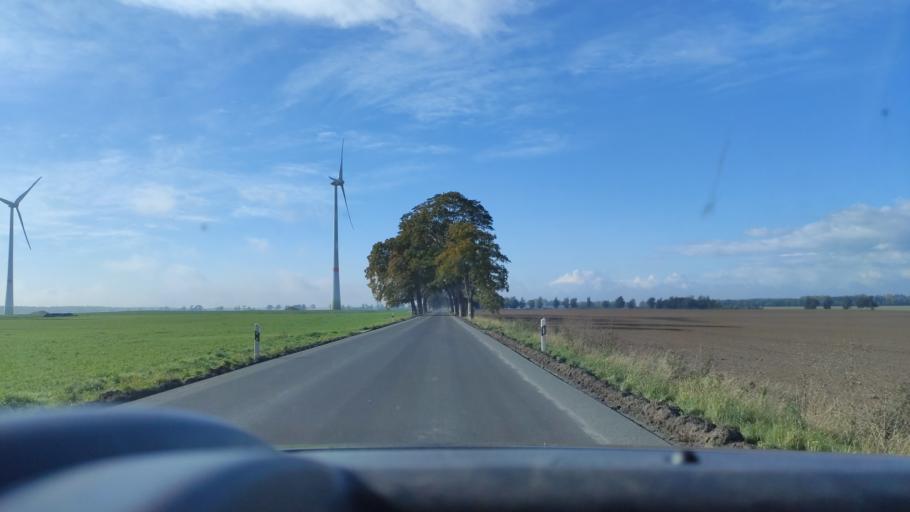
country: DE
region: Mecklenburg-Vorpommern
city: Grimmen
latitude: 54.0567
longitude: 13.1490
